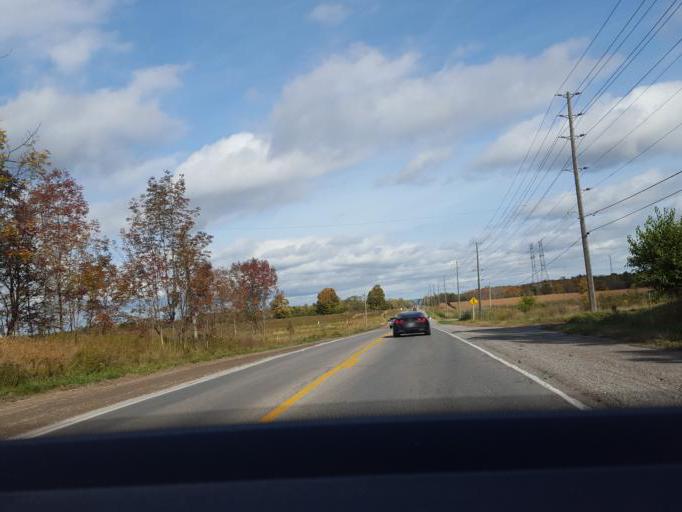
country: CA
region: Ontario
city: Oshawa
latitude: 43.9581
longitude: -78.7692
